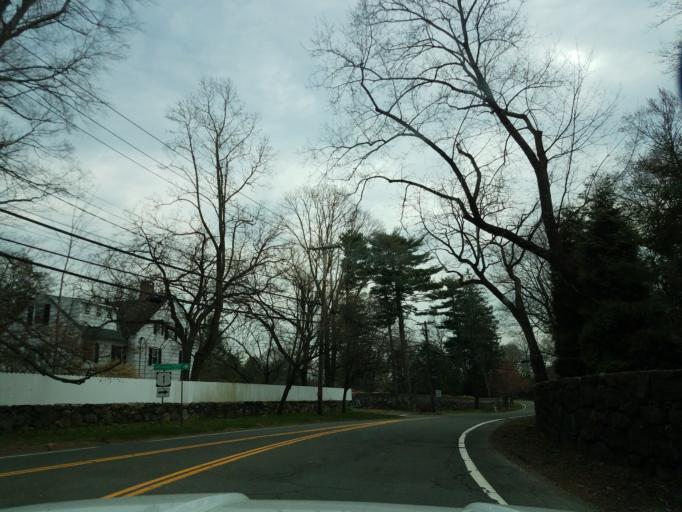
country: US
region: Connecticut
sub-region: Fairfield County
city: Greenwich
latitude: 41.0490
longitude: -73.6378
